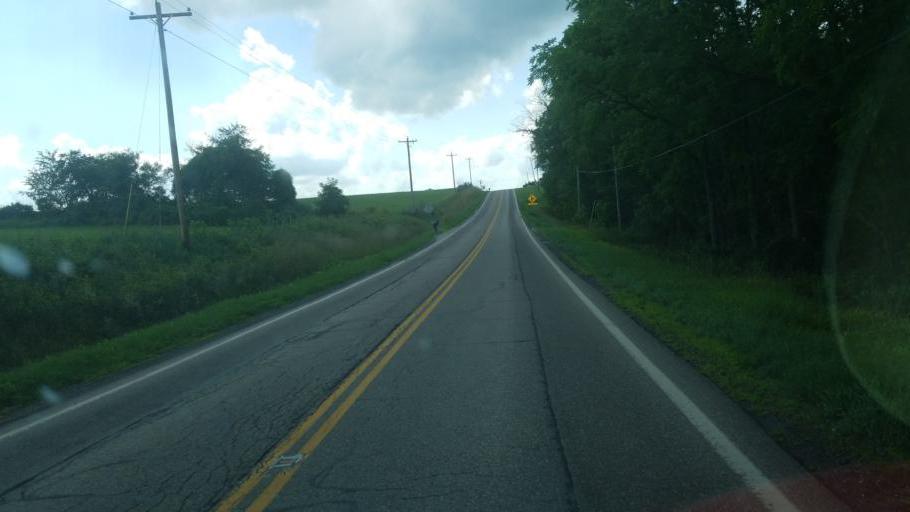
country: US
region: Ohio
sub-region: Knox County
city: Oak Hill
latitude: 40.3340
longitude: -82.2212
